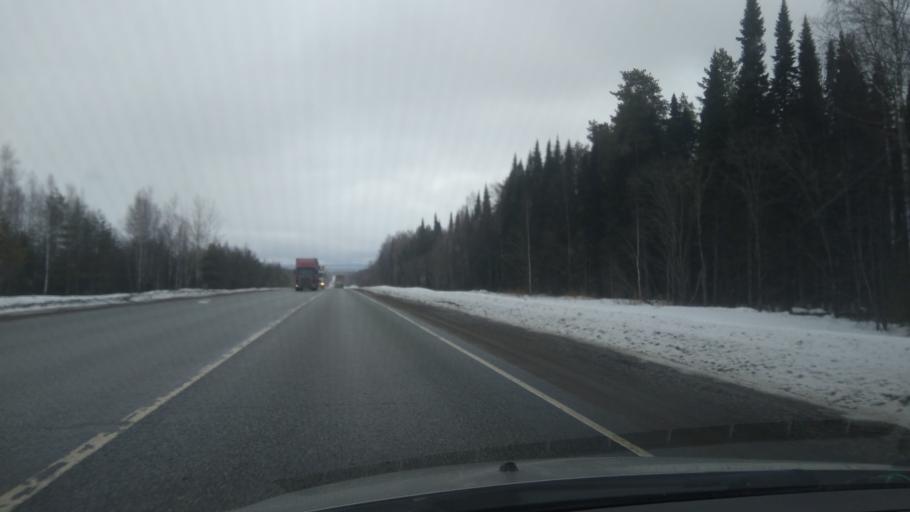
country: RU
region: Sverdlovsk
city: Achit
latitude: 56.8261
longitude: 57.7972
